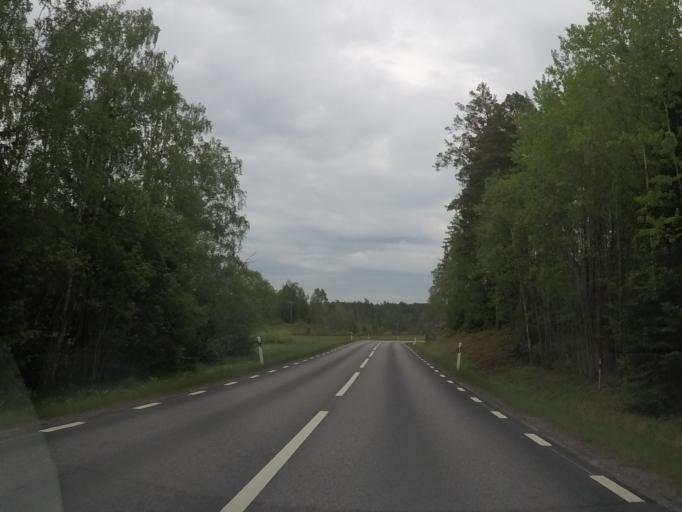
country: SE
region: Soedermanland
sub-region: Flens Kommun
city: Malmkoping
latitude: 59.0676
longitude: 16.7674
